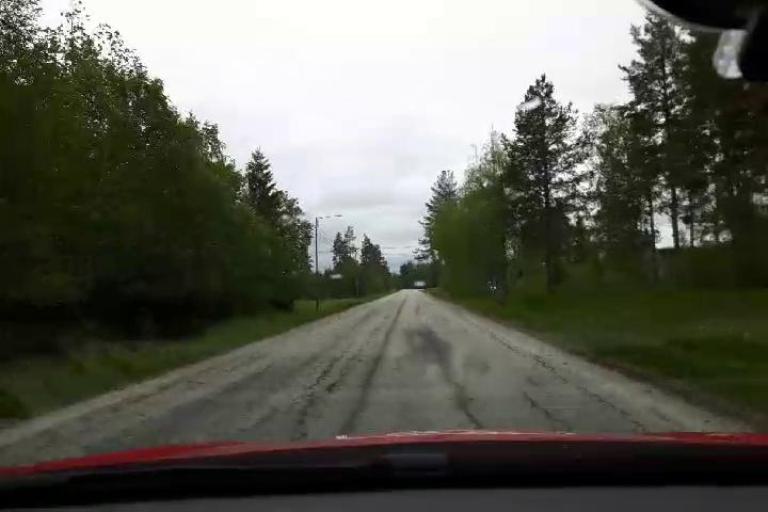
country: SE
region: Jaemtland
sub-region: Bergs Kommun
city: Hoverberg
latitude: 62.7401
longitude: 14.4231
